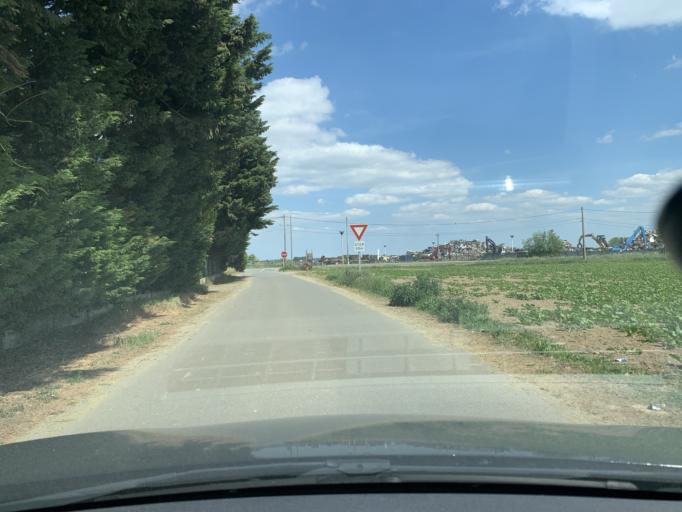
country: FR
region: Nord-Pas-de-Calais
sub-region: Departement du Nord
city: Aubigny-au-Bac
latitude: 50.2262
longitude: 3.1747
